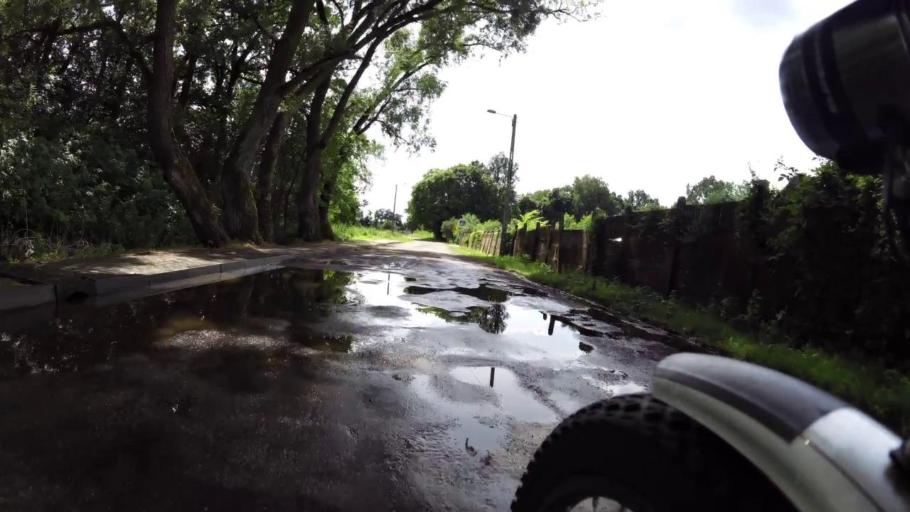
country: PL
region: West Pomeranian Voivodeship
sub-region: Powiat lobeski
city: Wegorzyno
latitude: 53.5180
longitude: 15.4484
